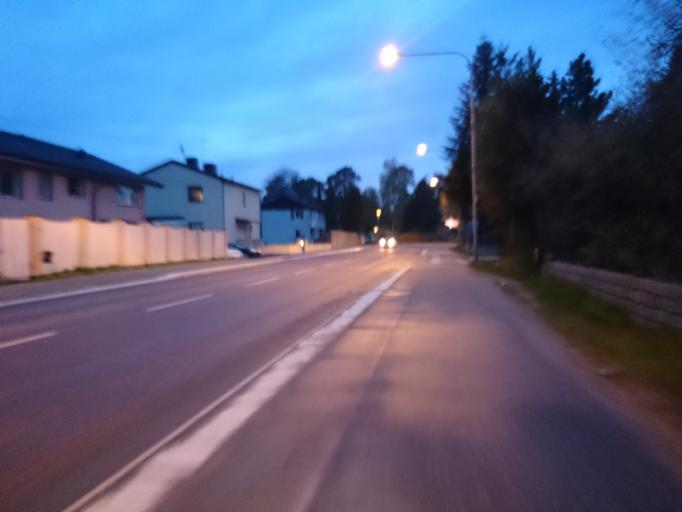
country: SE
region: Stockholm
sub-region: Huddinge Kommun
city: Segeltorp
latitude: 59.2720
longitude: 17.9535
